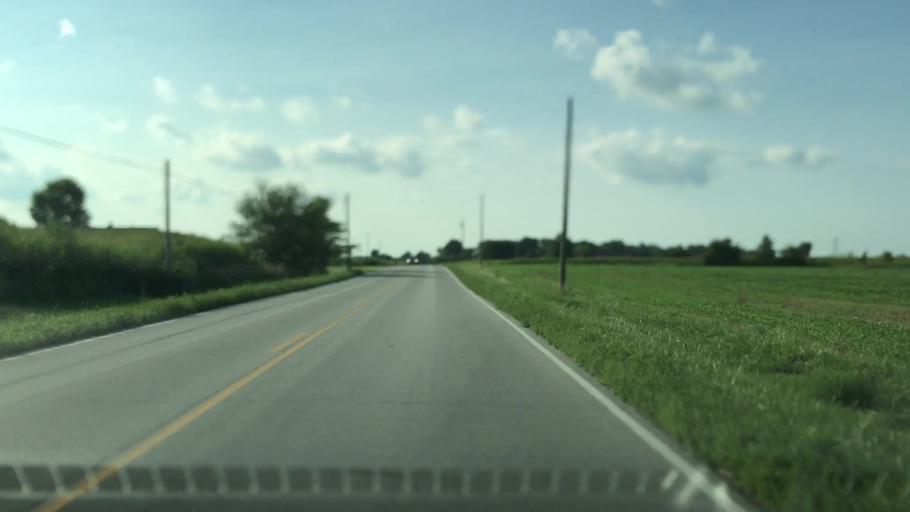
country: US
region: Ohio
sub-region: Union County
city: Marysville
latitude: 40.2009
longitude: -83.3451
